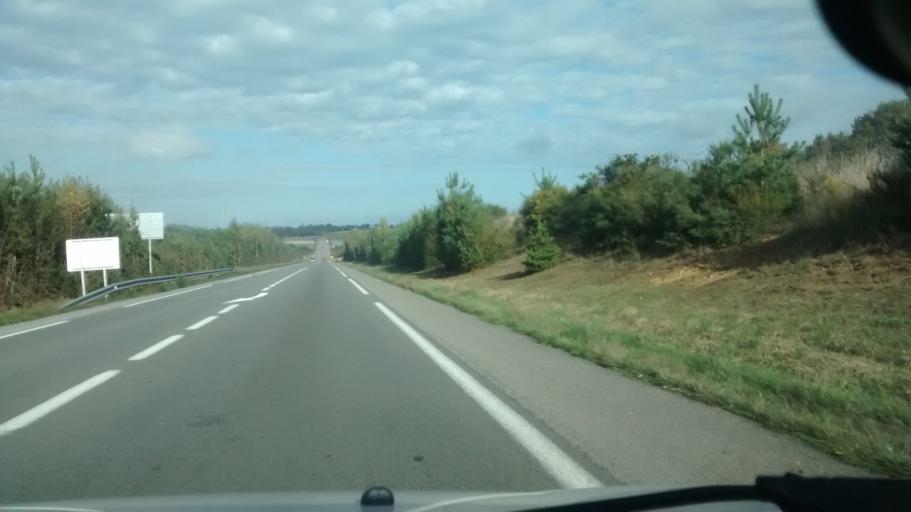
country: FR
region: Pays de la Loire
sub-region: Departement de Maine-et-Loire
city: Pouance
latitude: 47.7455
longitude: -1.2046
